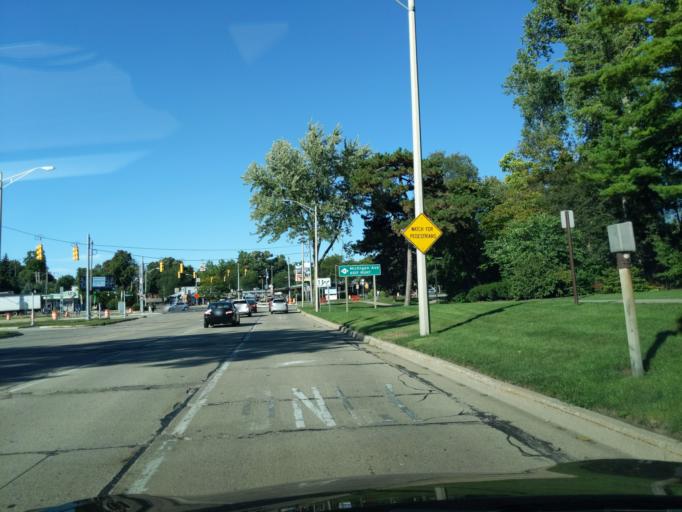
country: US
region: Michigan
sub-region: Ingham County
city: East Lansing
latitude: 42.7326
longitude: -84.4937
